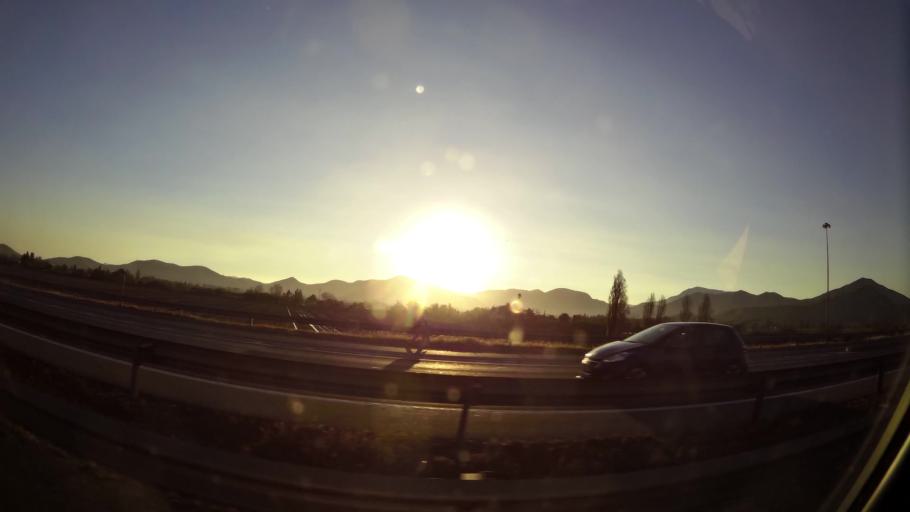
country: CL
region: Santiago Metropolitan
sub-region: Provincia de Santiago
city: Lo Prado
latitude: -33.5092
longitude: -70.7993
